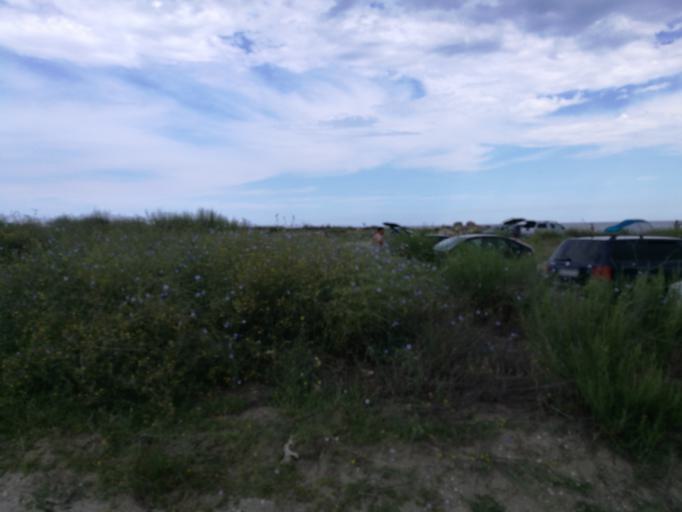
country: RO
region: Constanta
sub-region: Comuna Corbu
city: Corbu
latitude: 44.4301
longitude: 28.7677
